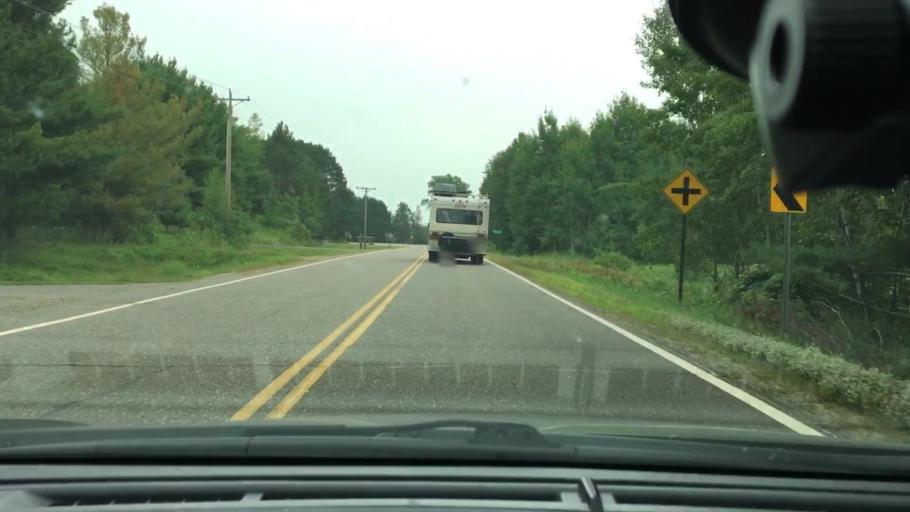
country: US
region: Minnesota
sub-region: Aitkin County
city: Aitkin
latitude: 46.4012
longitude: -93.7724
